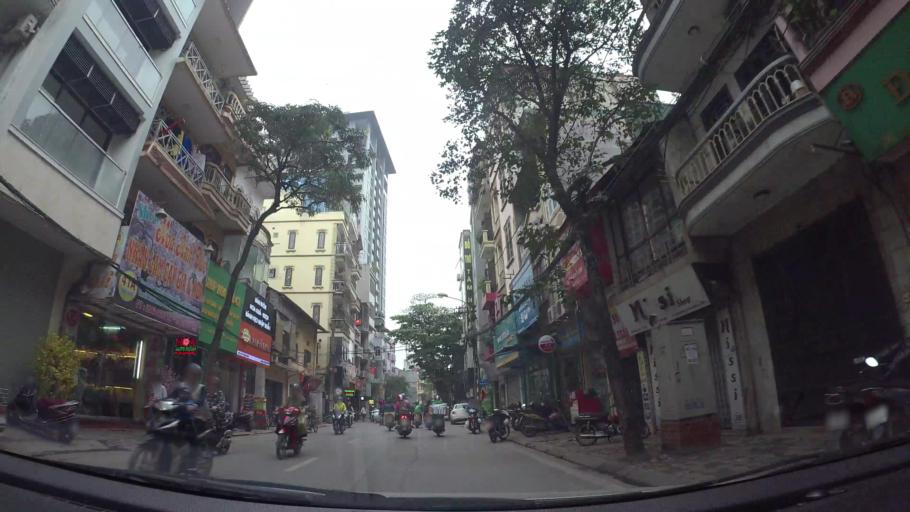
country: VN
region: Ha Noi
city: Dong Da
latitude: 21.0411
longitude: 105.8275
